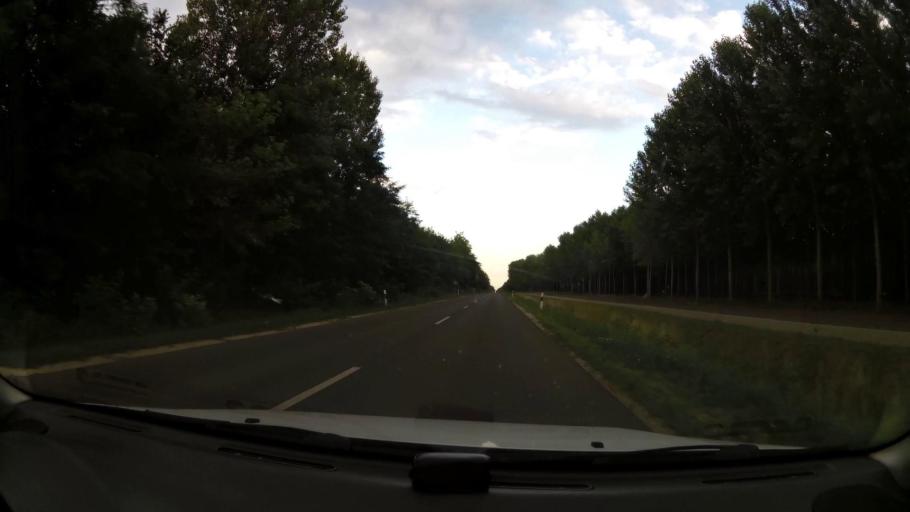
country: HU
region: Pest
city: Ujszilvas
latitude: 47.2911
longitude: 19.9044
